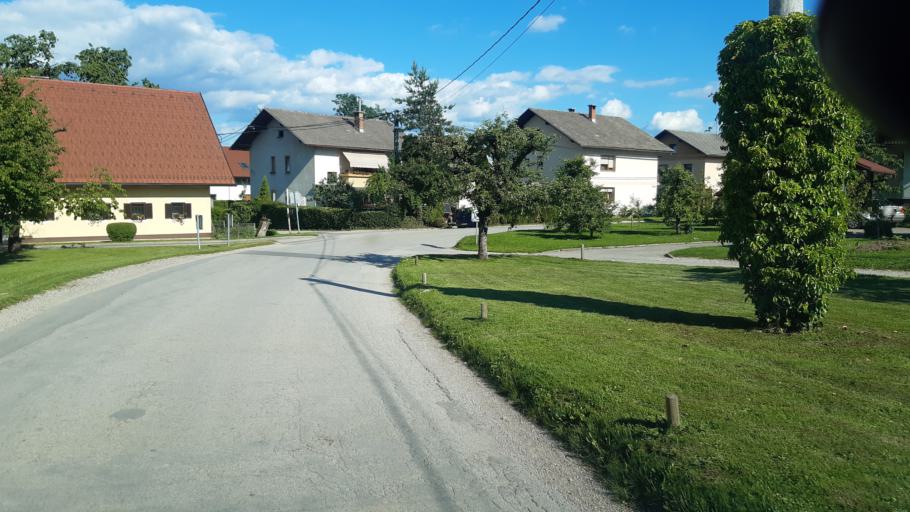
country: SI
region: Sencur
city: Hrastje
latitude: 46.1957
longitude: 14.4009
